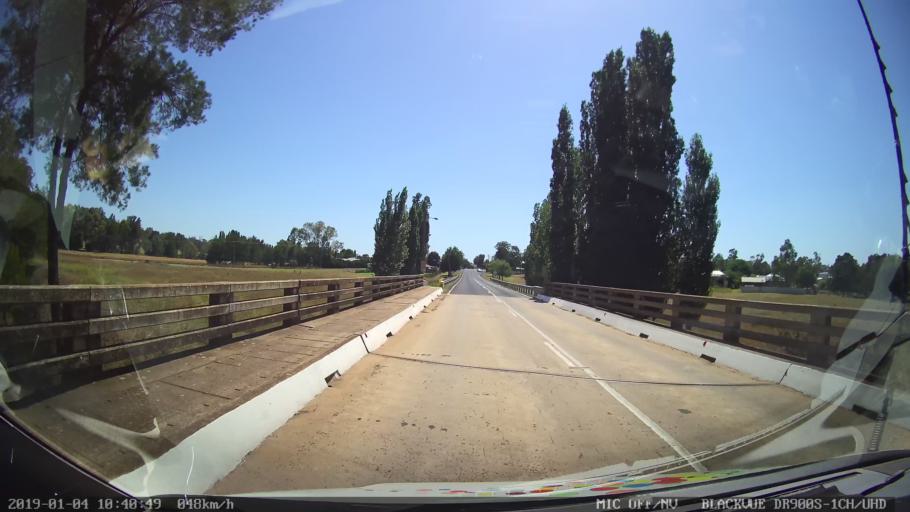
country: AU
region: New South Wales
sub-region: Cabonne
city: Molong
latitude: -33.2885
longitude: 148.7346
